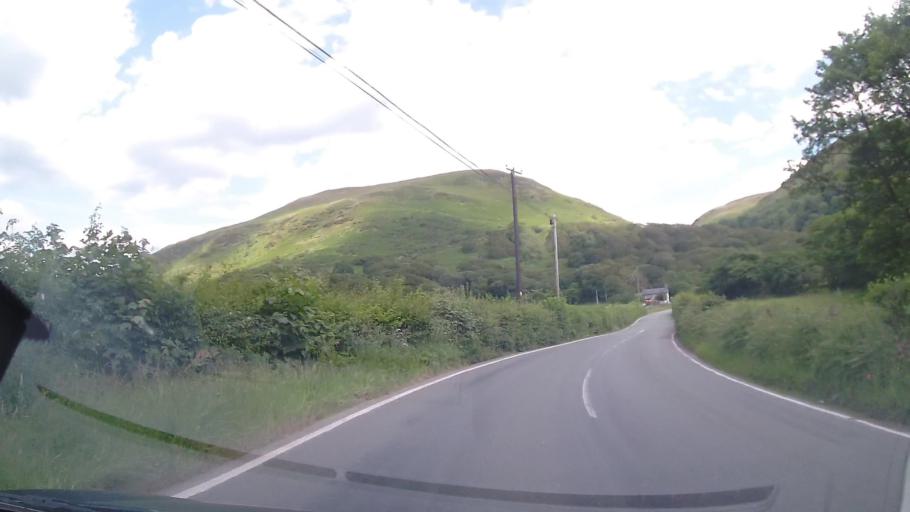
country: GB
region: Wales
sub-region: Gwynedd
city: Tywyn
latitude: 52.6236
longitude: -3.9992
